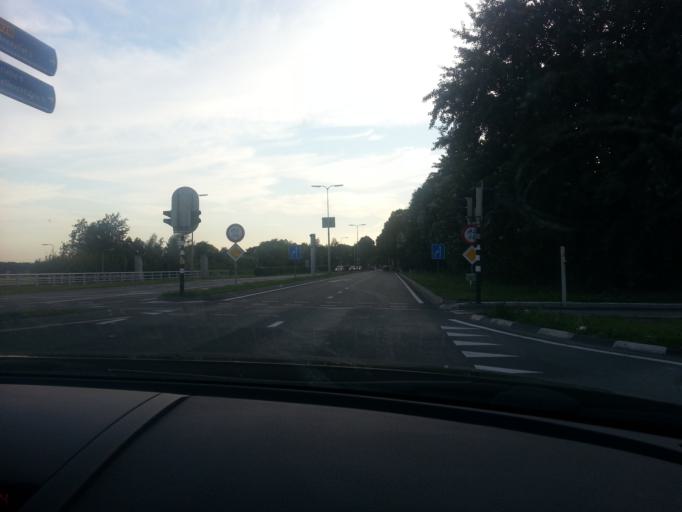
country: NL
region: South Holland
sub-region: Gemeente Maassluis
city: Maassluis
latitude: 51.8589
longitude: 4.2621
